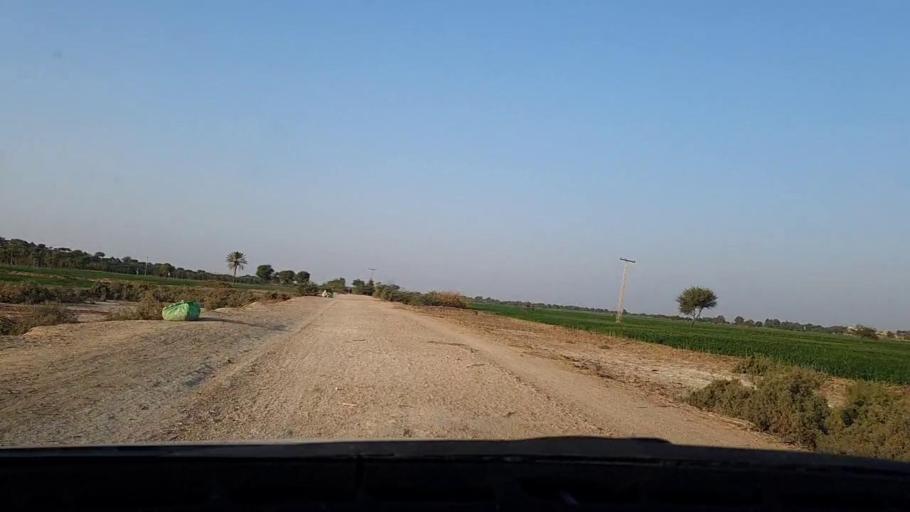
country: PK
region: Sindh
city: Tando Mittha Khan
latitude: 25.8581
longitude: 69.2725
